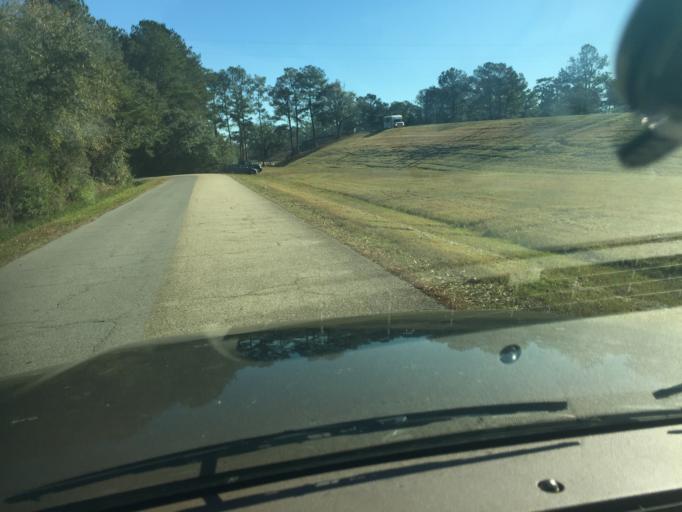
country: US
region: Louisiana
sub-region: Saint Tammany Parish
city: Slidell
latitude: 30.3108
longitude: -89.7420
